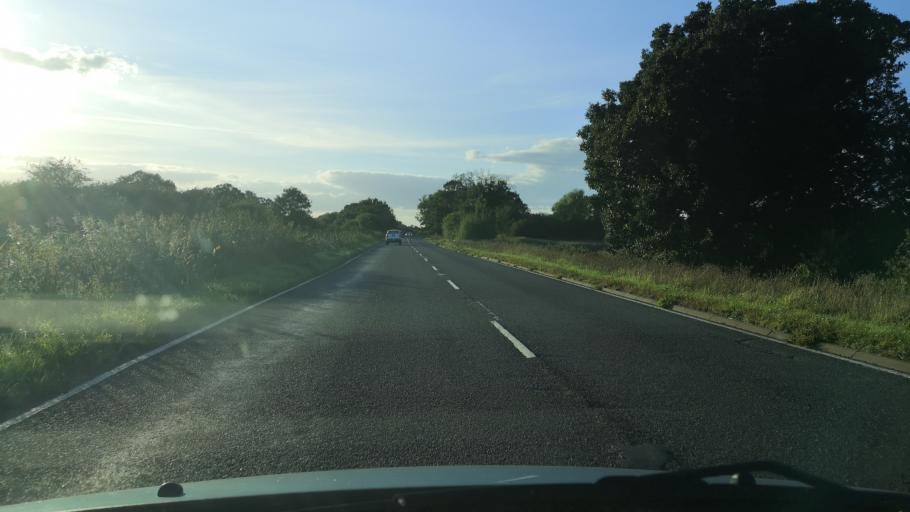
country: GB
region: England
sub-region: North Lincolnshire
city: Belton
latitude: 53.5824
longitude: -0.8045
